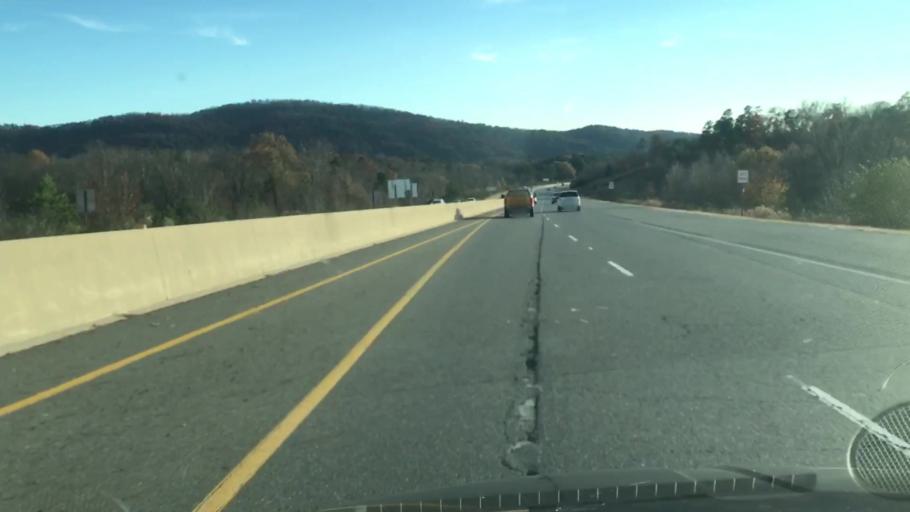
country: US
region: Arkansas
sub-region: Garland County
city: Hot Springs
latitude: 34.4999
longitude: -92.9755
